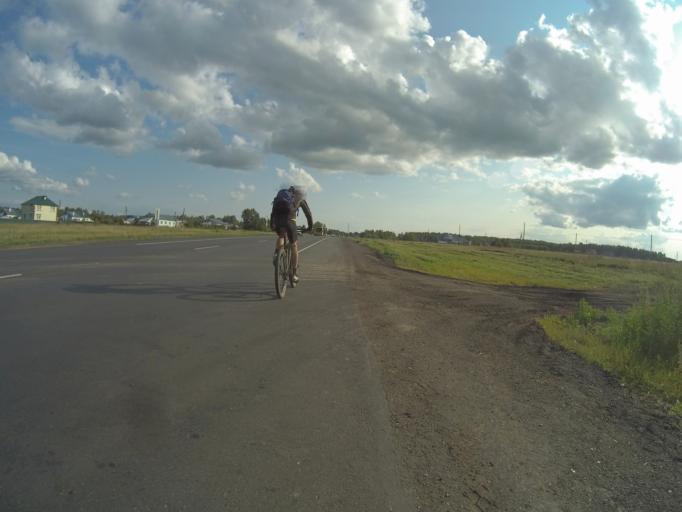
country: RU
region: Vladimir
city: Kideksha
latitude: 56.5069
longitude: 40.5441
